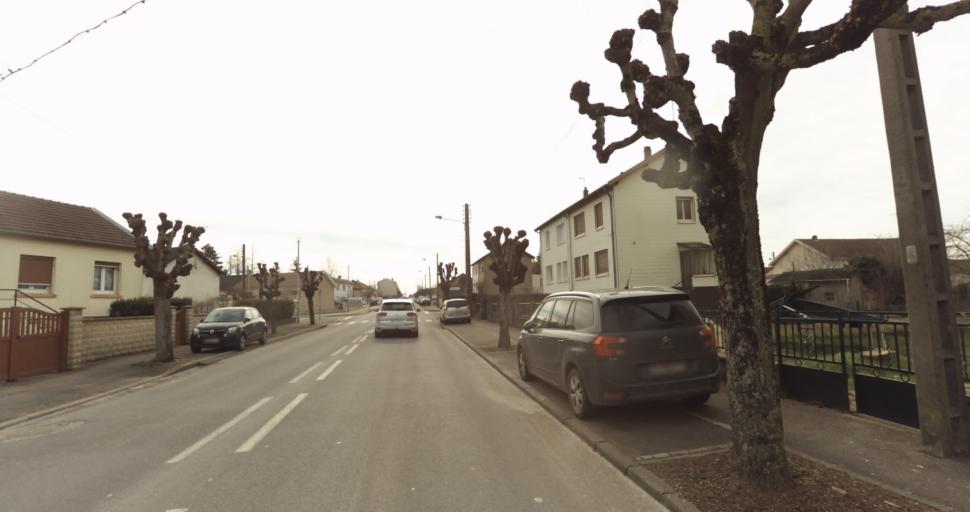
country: FR
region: Lorraine
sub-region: Departement de Meurthe-et-Moselle
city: Jarny
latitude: 49.1548
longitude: 5.8802
